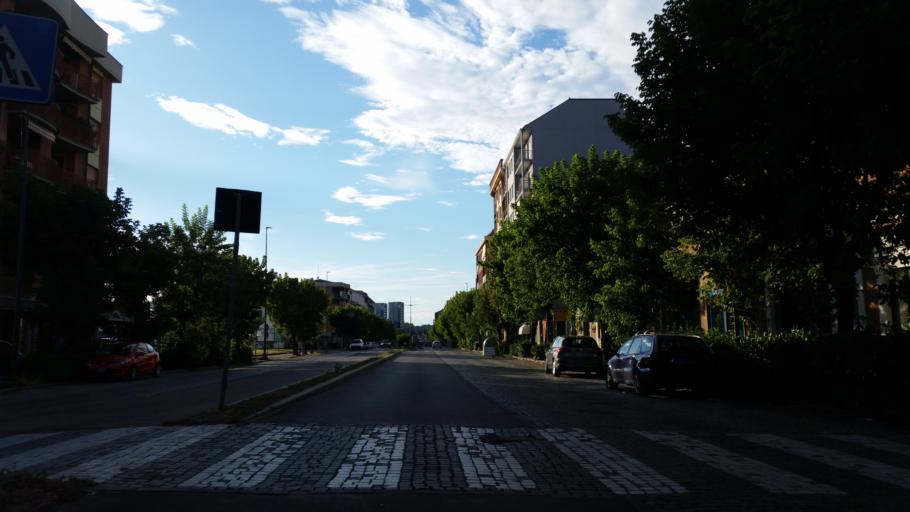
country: IT
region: Piedmont
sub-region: Provincia di Asti
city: Asti
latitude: 44.9012
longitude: 8.1925
